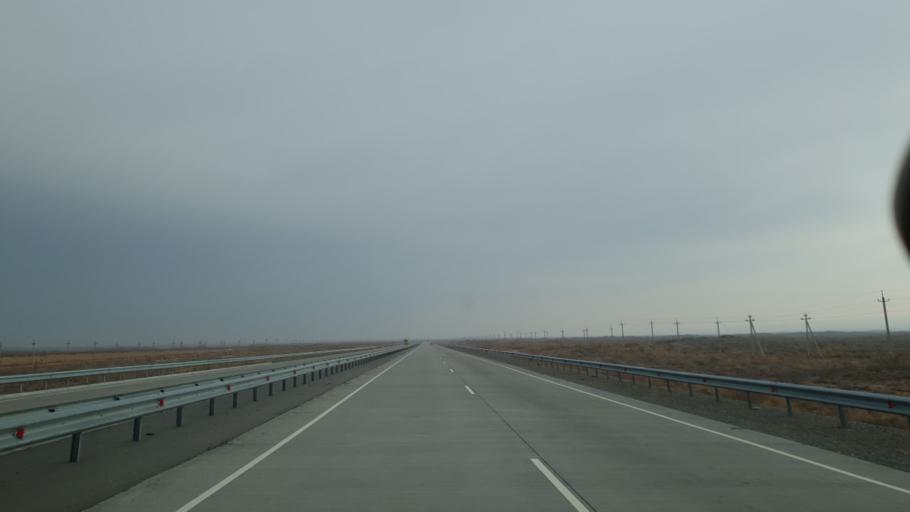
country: KZ
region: Almaty Oblysy
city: Kegen
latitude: 43.7368
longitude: 78.8068
